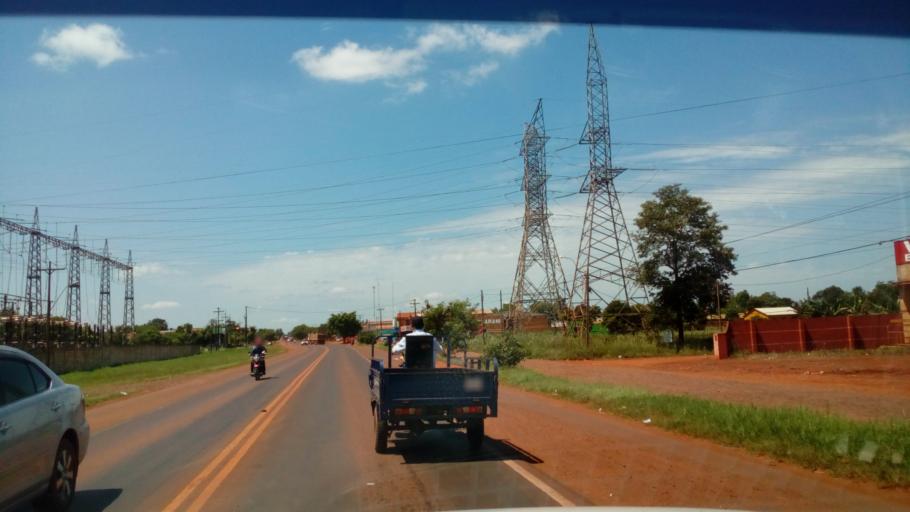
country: PY
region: Alto Parana
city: Colonia Yguazu
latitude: -25.4873
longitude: -54.8978
